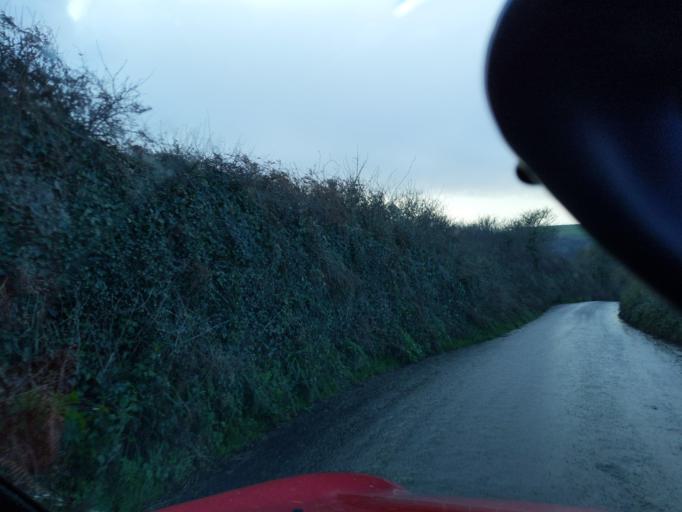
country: GB
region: England
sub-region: Cornwall
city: Looe
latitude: 50.3398
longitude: -4.4835
